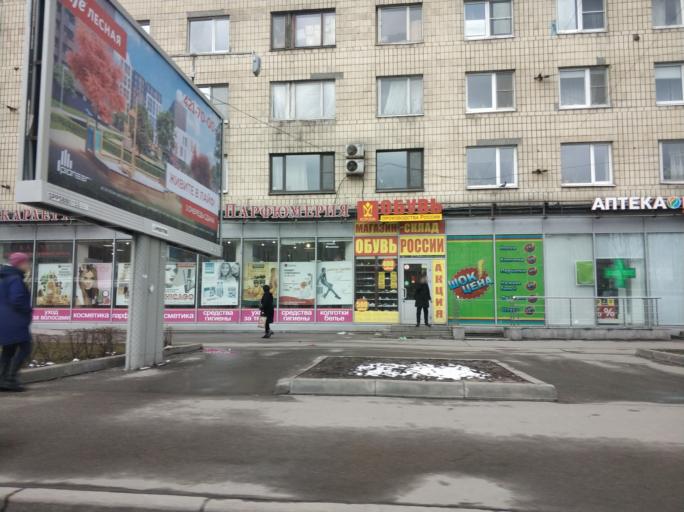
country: RU
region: St.-Petersburg
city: Kushelevka
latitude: 60.0011
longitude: 30.3656
